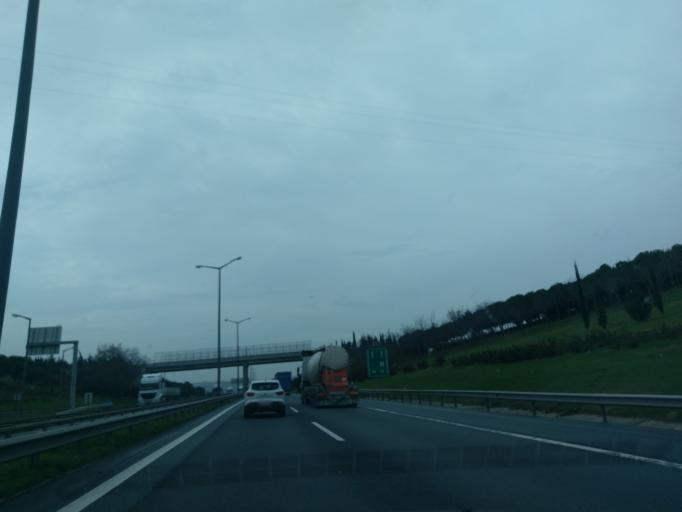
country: TR
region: Istanbul
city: Silivri
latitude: 41.1126
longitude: 28.2629
